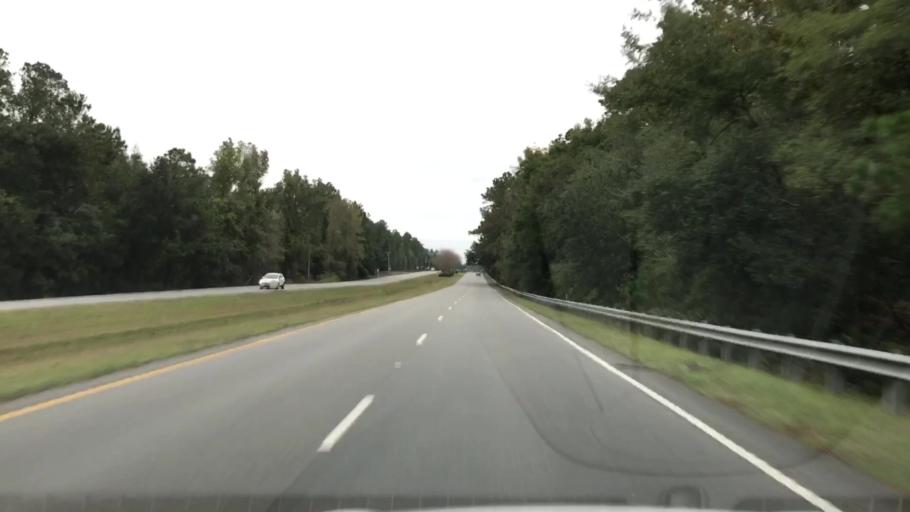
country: US
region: South Carolina
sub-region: Georgetown County
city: Georgetown
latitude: 33.2139
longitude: -79.3808
